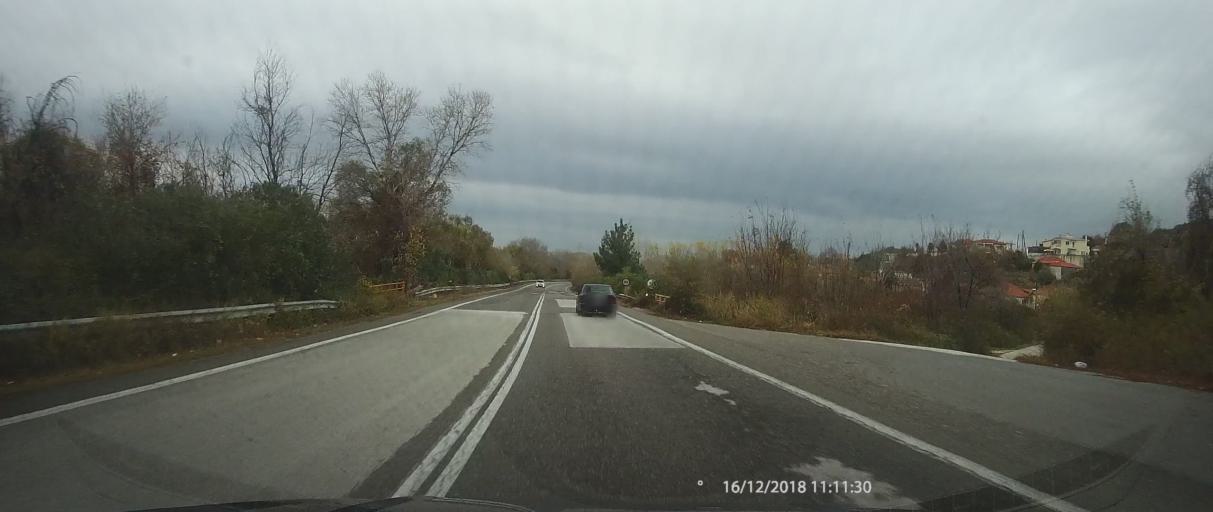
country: GR
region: East Macedonia and Thrace
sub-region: Nomos Xanthis
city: Petrochori
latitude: 41.0846
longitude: 24.7638
